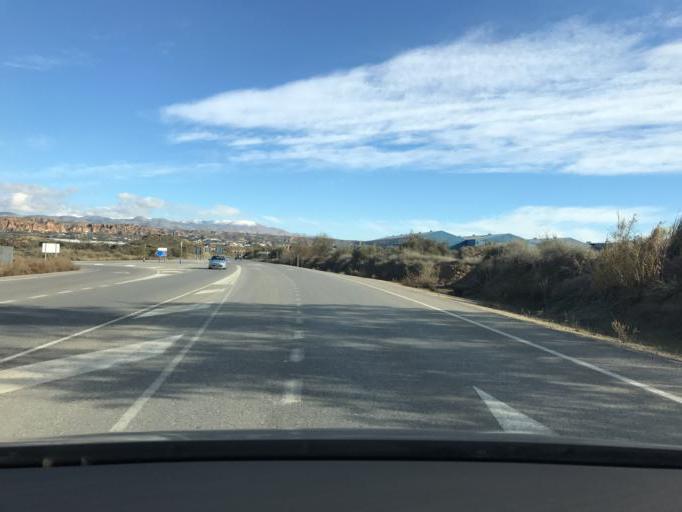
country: ES
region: Andalusia
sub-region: Provincia de Granada
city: Guadix
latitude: 37.3169
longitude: -3.1615
